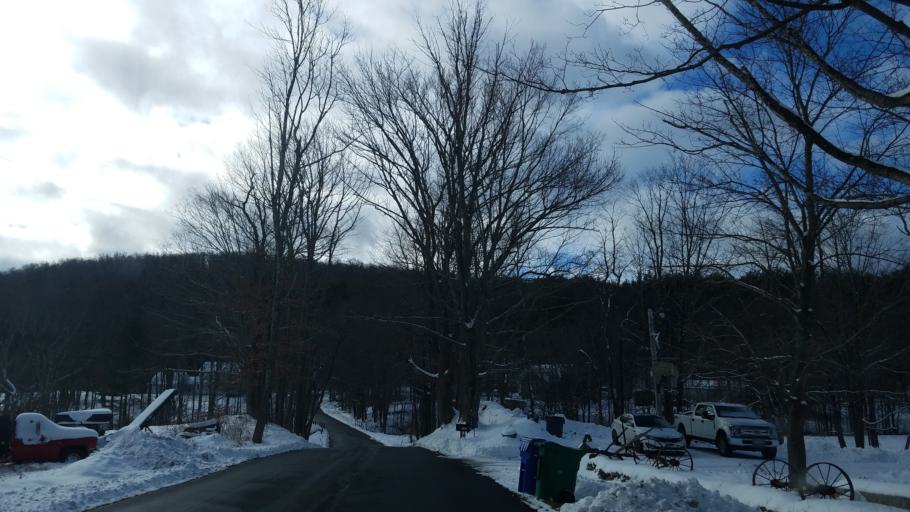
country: US
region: Connecticut
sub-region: Litchfield County
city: Winchester Center
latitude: 41.9624
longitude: -73.1199
